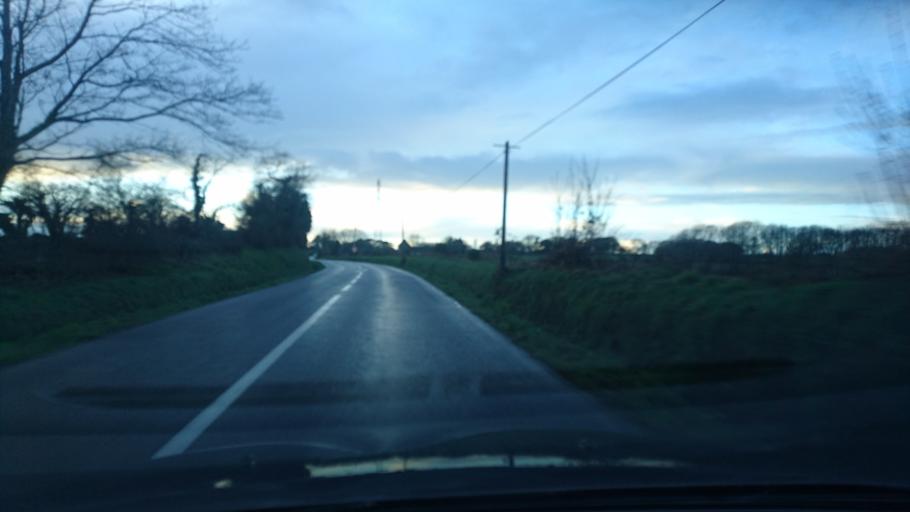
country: FR
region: Brittany
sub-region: Departement du Finistere
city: Guilers
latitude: 48.4103
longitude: -4.5540
